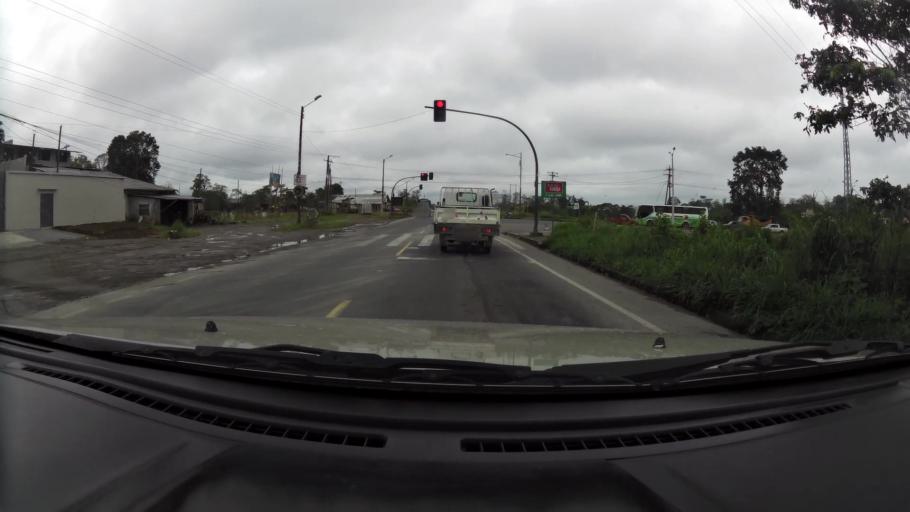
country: EC
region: Santo Domingo de los Tsachilas
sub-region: Canton Santo Domingo de los Colorados
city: Santo Domingo de los Colorados
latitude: -0.2748
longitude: -79.1647
